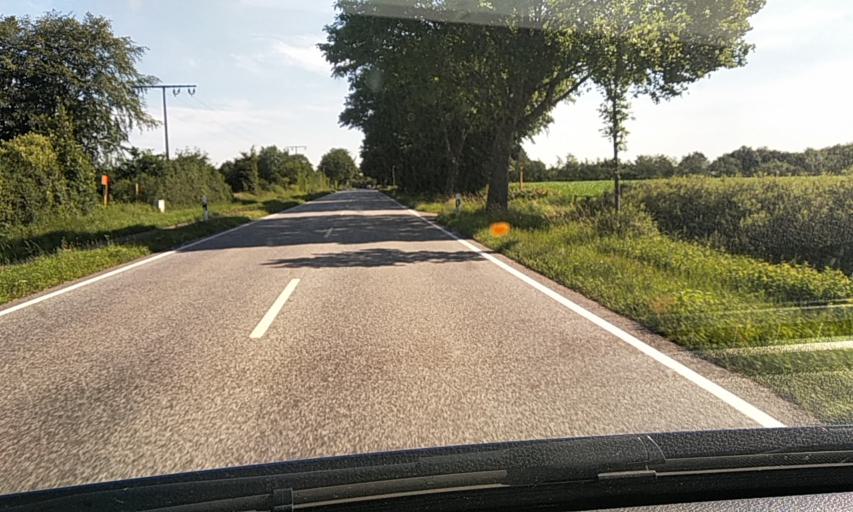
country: DE
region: Schleswig-Holstein
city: Fockbek
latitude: 54.2947
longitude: 9.5865
